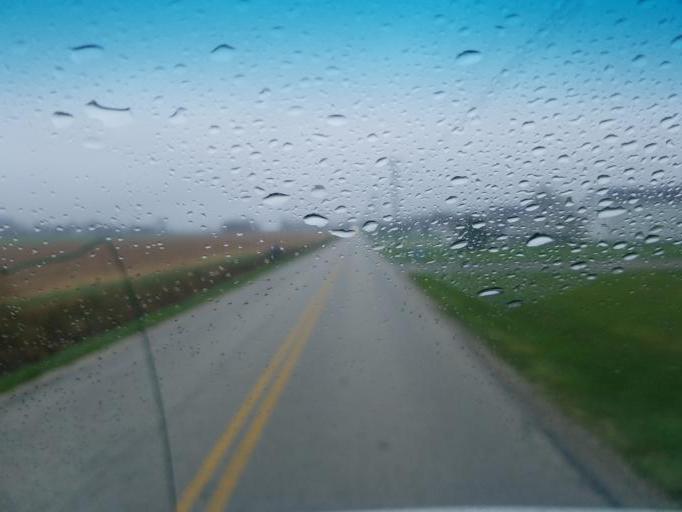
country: US
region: Ohio
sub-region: Wood County
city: North Baltimore
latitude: 41.1514
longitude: -83.6313
